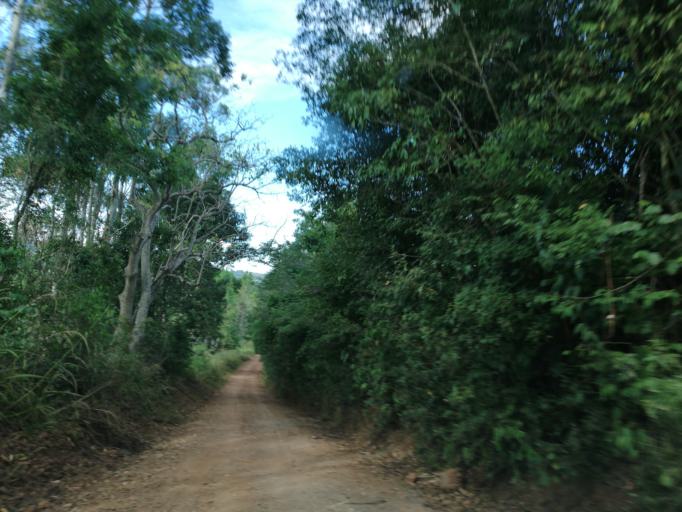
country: AR
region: Misiones
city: Dos de Mayo
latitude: -27.0156
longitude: -54.4253
